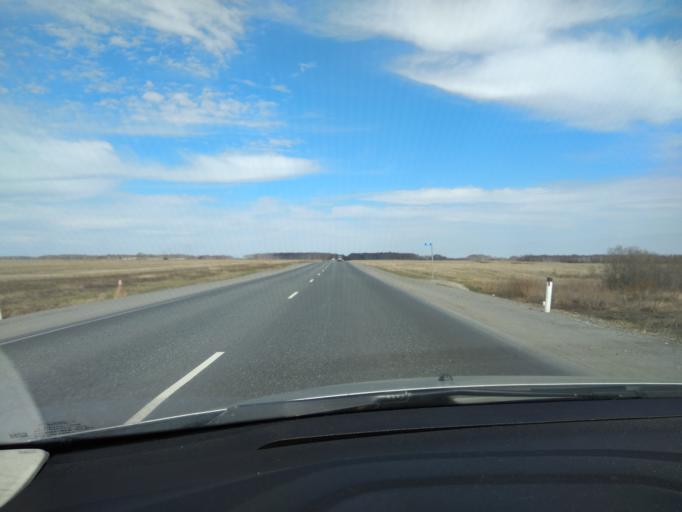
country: RU
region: Sverdlovsk
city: Pyshma
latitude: 56.9194
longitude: 63.1354
